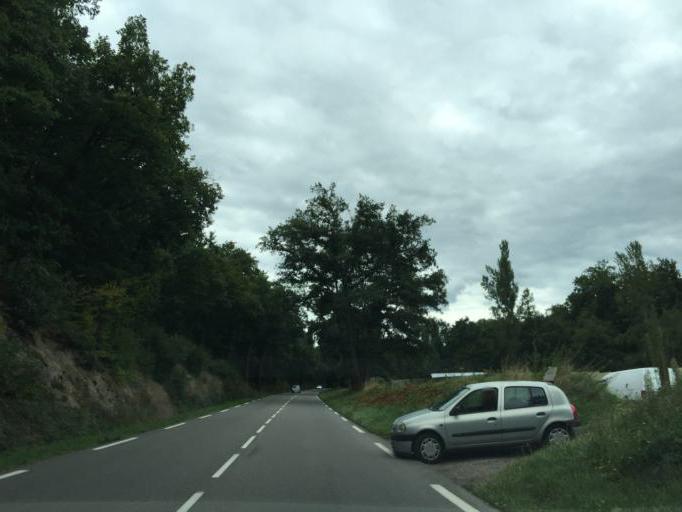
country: FR
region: Rhone-Alpes
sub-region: Departement de la Loire
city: La Talaudiere
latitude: 45.4728
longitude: 4.4124
